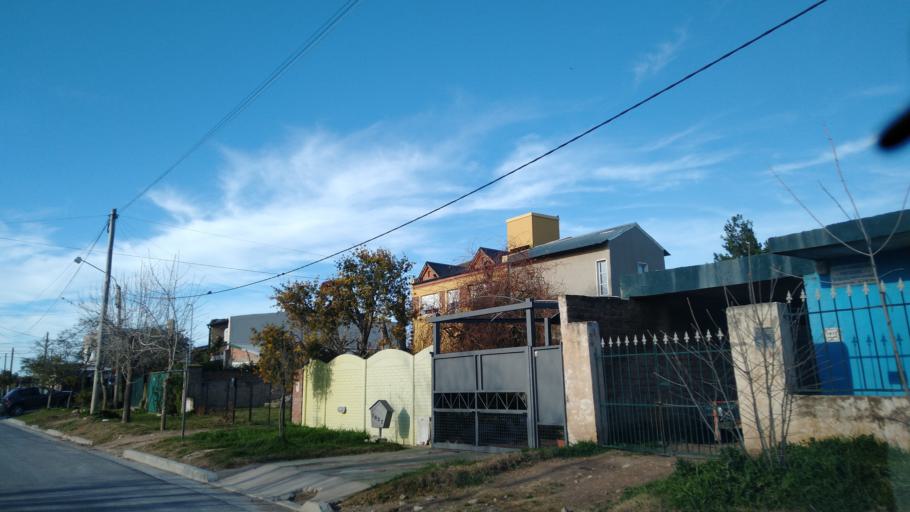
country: AR
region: Buenos Aires
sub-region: Partido de Bahia Blanca
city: Bahia Blanca
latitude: -38.7033
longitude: -62.2077
